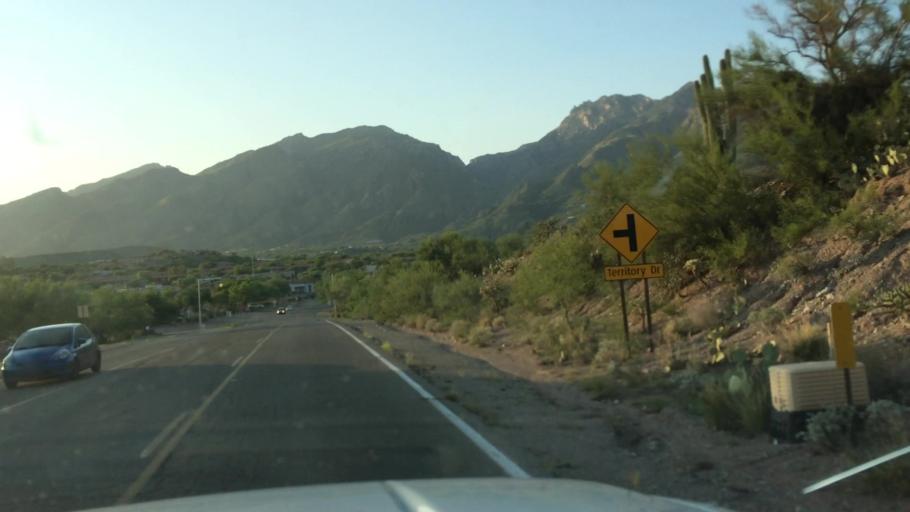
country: US
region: Arizona
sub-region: Pima County
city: Catalina Foothills
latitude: 32.3052
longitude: -110.8429
